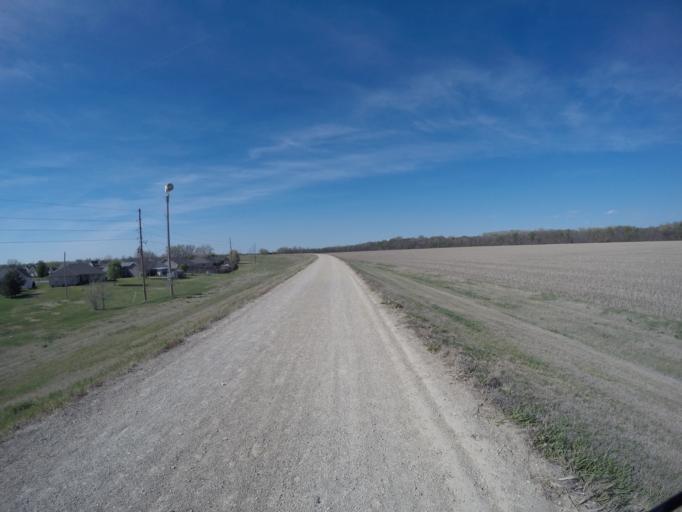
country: US
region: Kansas
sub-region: Saline County
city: Salina
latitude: 38.8169
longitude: -97.5826
